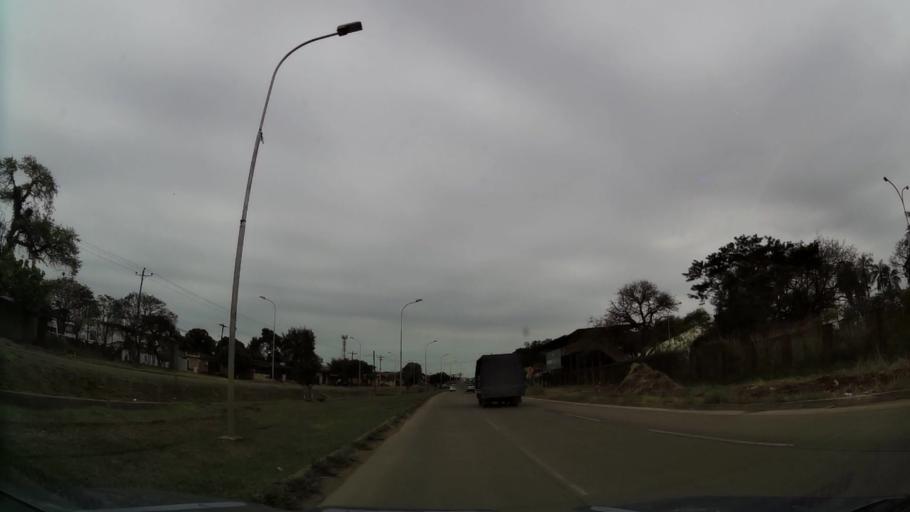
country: BO
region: Santa Cruz
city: Santa Cruz de la Sierra
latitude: -17.8326
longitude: -63.1922
